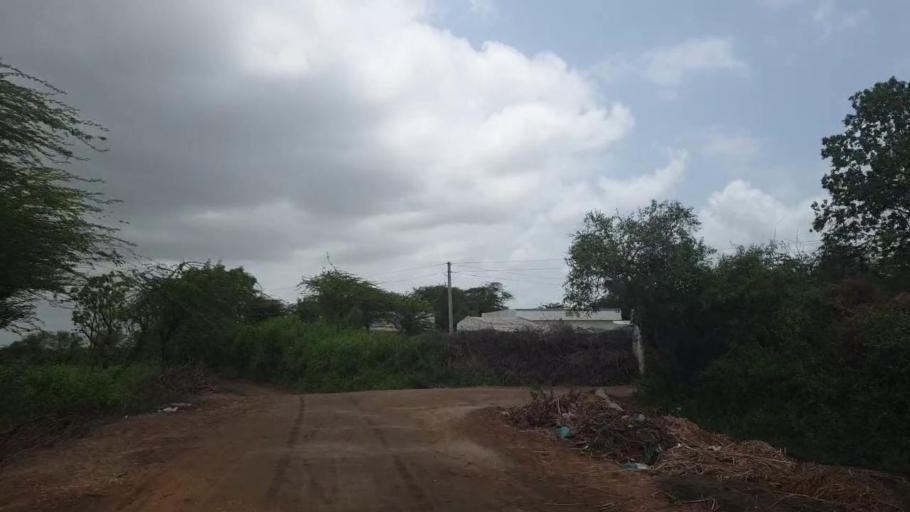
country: PK
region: Sindh
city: Badin
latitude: 24.6706
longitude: 68.9055
